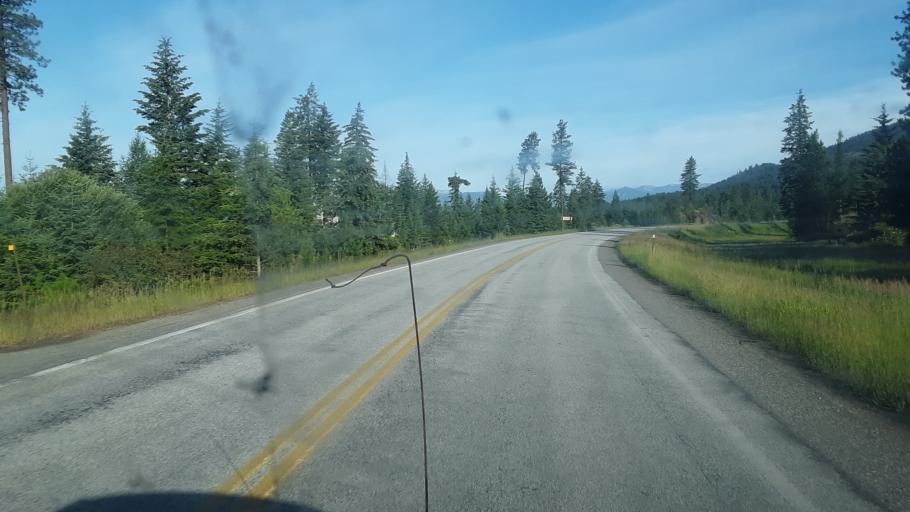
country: US
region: Idaho
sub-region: Boundary County
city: Bonners Ferry
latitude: 48.7221
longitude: -116.1672
